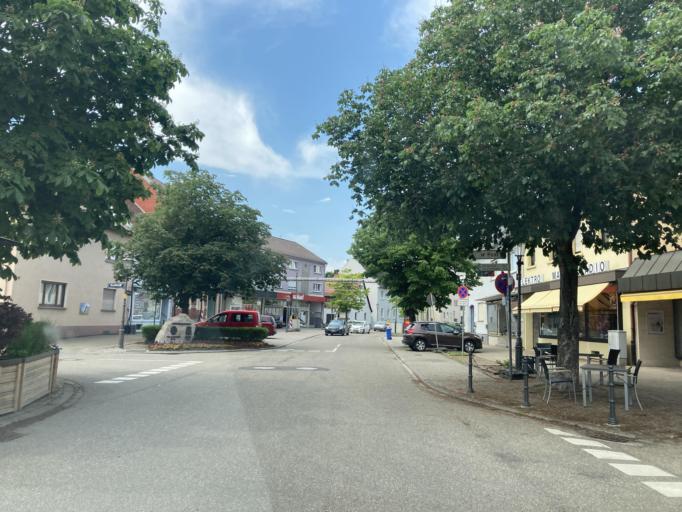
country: DE
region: Baden-Wuerttemberg
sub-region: Karlsruhe Region
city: Weingarten
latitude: 49.0535
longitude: 8.5269
